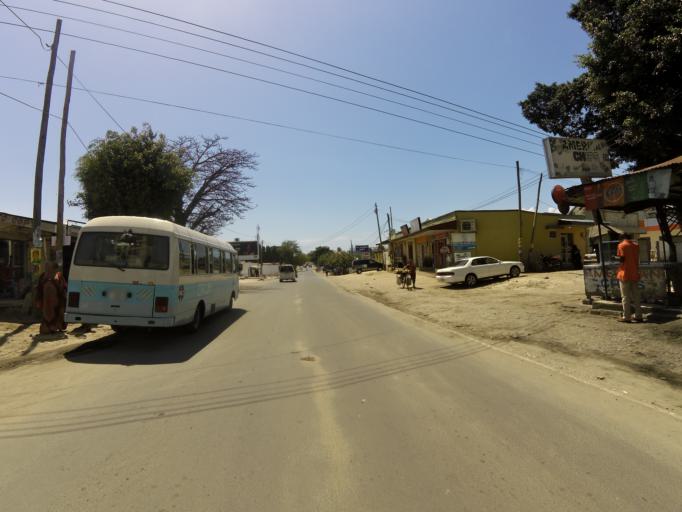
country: TZ
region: Dar es Salaam
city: Magomeni
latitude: -6.7898
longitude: 39.2659
